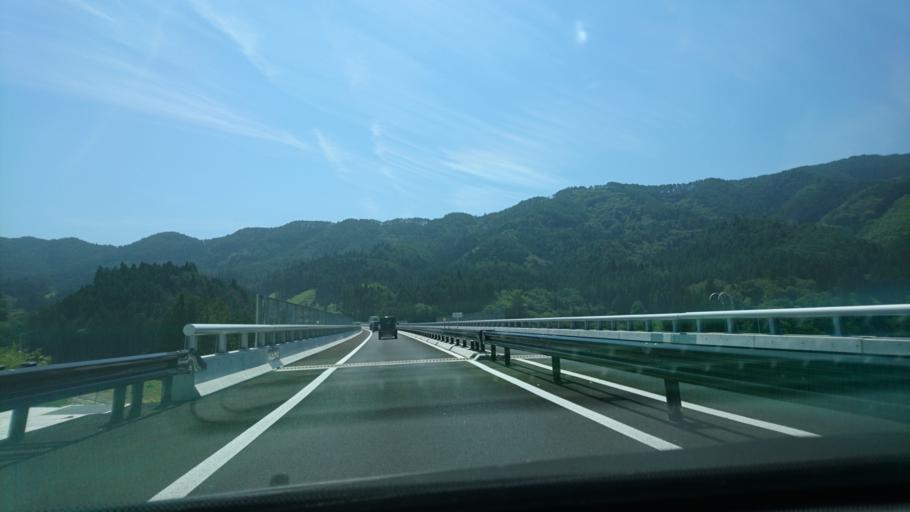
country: JP
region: Iwate
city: Ofunato
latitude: 38.9930
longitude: 141.6134
